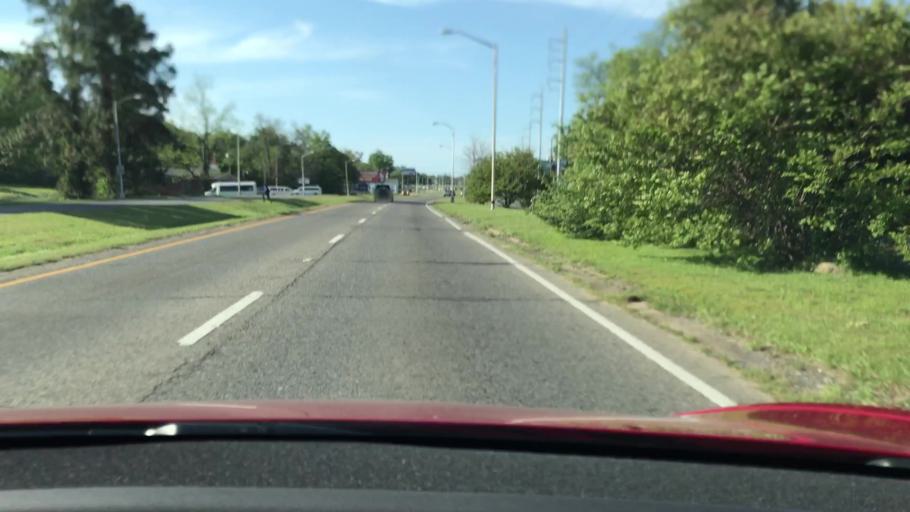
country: US
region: Louisiana
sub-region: Bossier Parish
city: Bossier City
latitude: 32.4873
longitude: -93.7241
